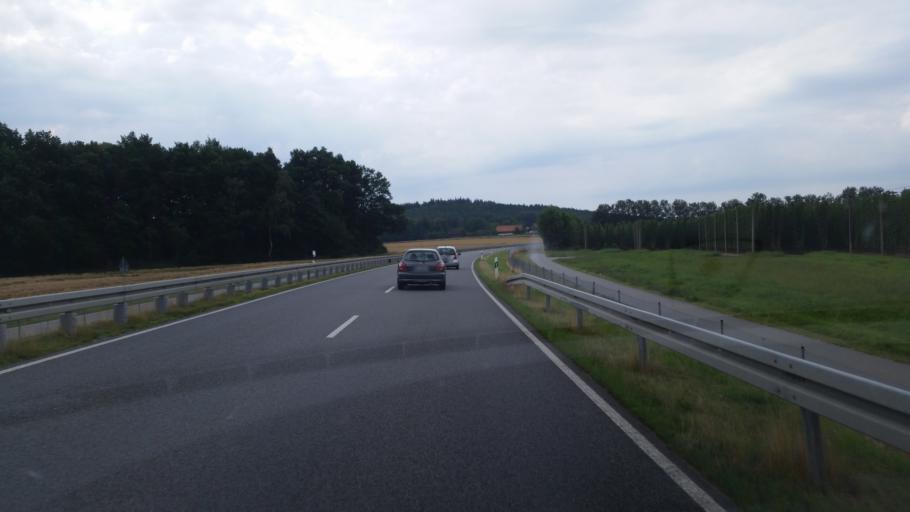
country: DE
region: Saxony
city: Elstra
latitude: 51.2178
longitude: 14.1534
